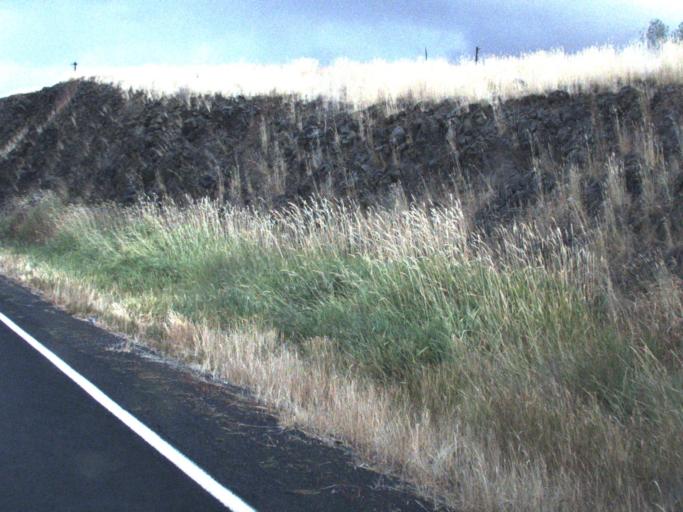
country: US
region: Washington
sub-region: Spokane County
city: Medical Lake
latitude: 47.7160
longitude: -117.8716
